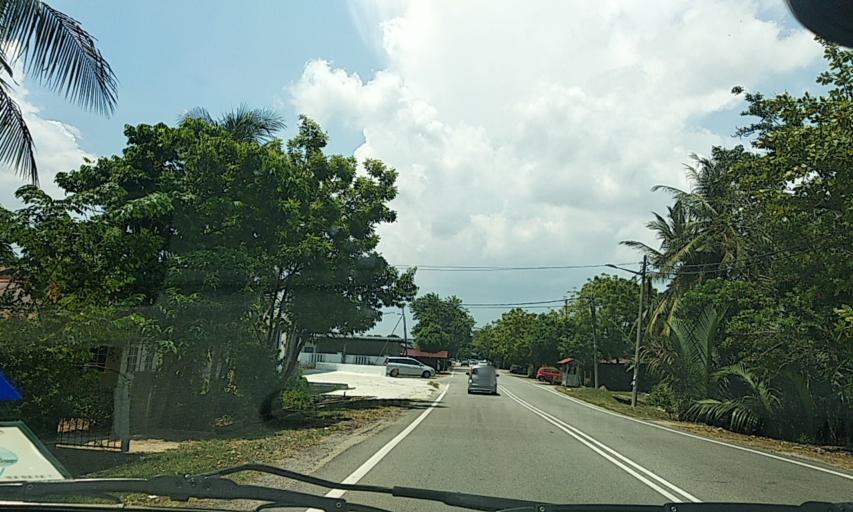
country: MY
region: Kedah
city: Sungai Petani
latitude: 5.6347
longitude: 100.4793
